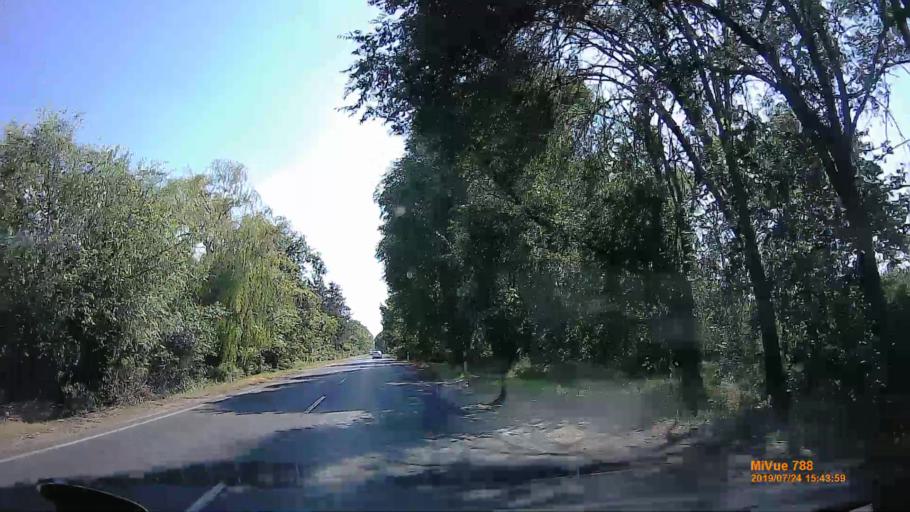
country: HU
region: Szabolcs-Szatmar-Bereg
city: Vasarosnameny
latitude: 48.1055
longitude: 22.3005
